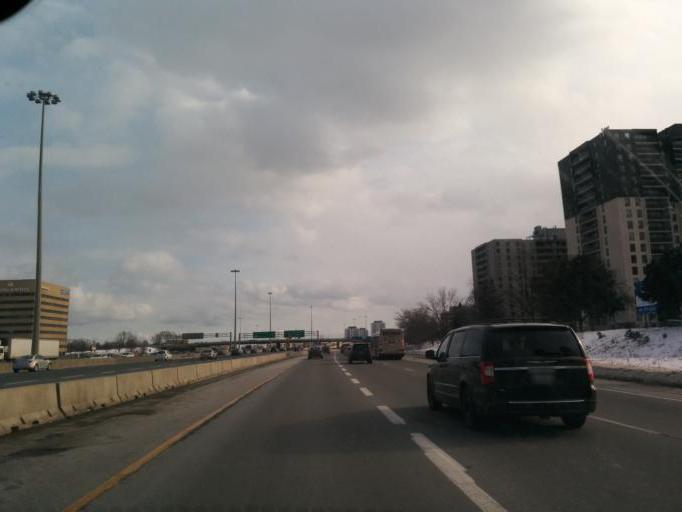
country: CA
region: Ontario
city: Etobicoke
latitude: 43.6399
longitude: -79.5612
